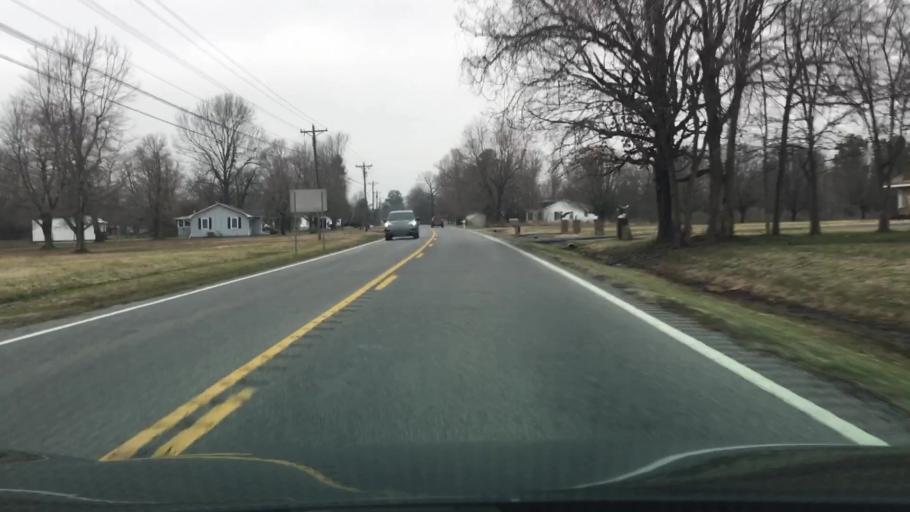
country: US
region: Kentucky
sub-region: Marshall County
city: Calvert City
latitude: 36.9690
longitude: -88.3872
